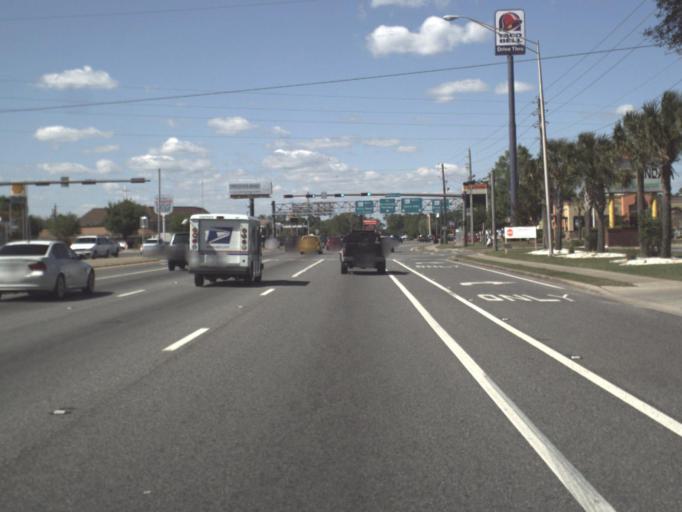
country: US
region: Florida
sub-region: Escambia County
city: Ferry Pass
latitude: 30.5071
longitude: -87.2213
